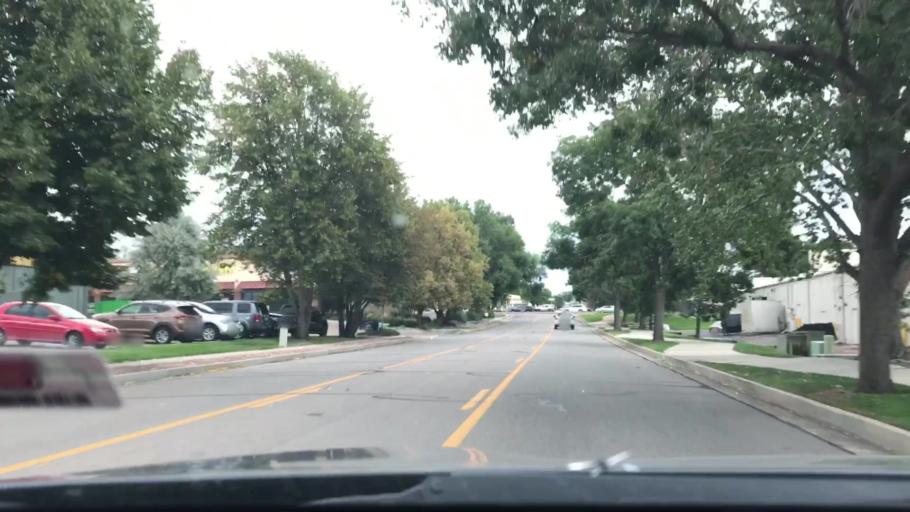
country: US
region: Colorado
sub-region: El Paso County
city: Cimarron Hills
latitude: 38.8898
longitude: -104.7590
